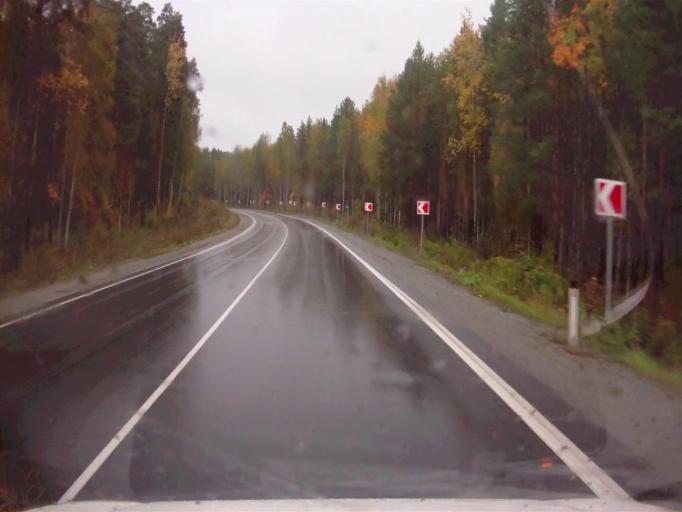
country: RU
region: Chelyabinsk
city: Tayginka
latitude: 55.6338
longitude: 60.5995
